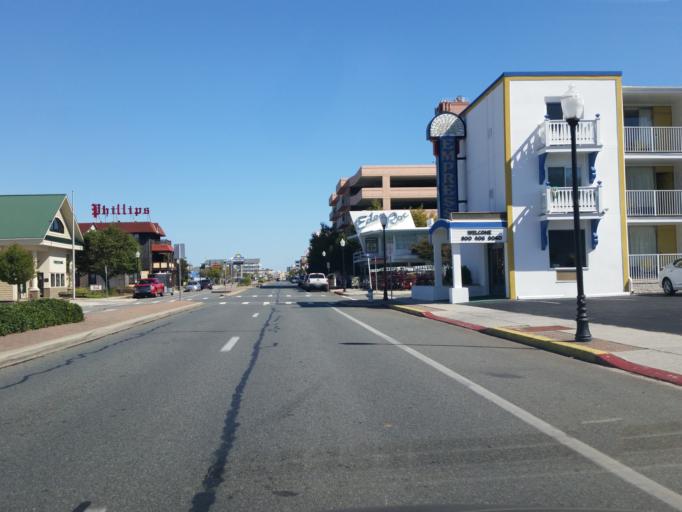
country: US
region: Maryland
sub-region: Worcester County
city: Ocean City
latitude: 38.3490
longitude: -75.0772
